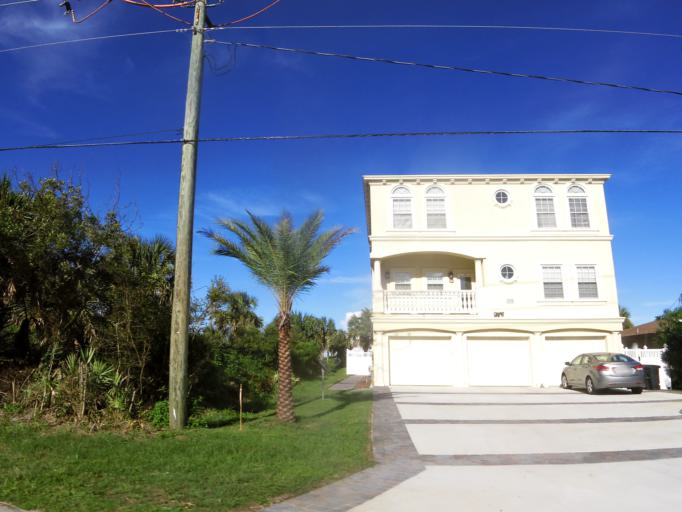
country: US
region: Florida
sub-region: Flagler County
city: Flagler Beach
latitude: 29.4881
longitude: -81.1319
